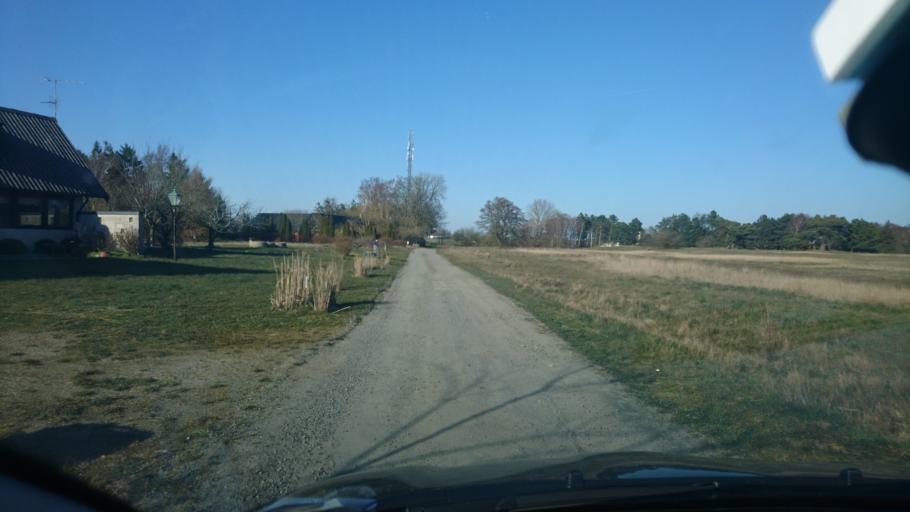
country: SE
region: Skane
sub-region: Simrishamns Kommun
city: Simrishamn
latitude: 55.4197
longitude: 14.2069
